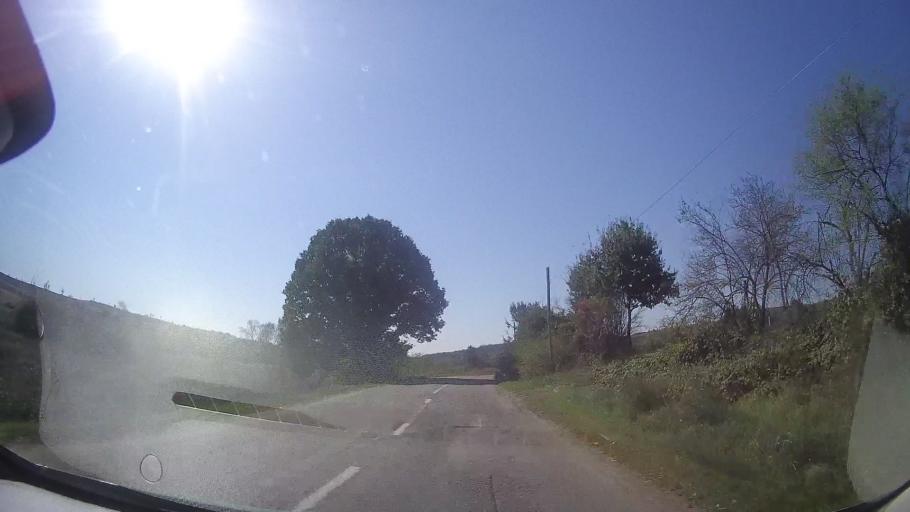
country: RO
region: Timis
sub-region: Comuna Ohaba Lunga
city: Ohaba Lunga
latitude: 45.9013
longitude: 21.9778
